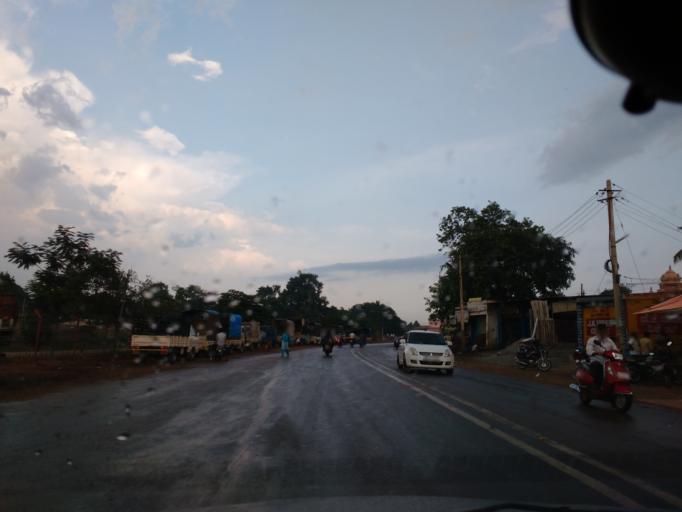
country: IN
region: Karnataka
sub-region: Tumkur
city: Tiptur
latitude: 13.2585
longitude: 76.4824
